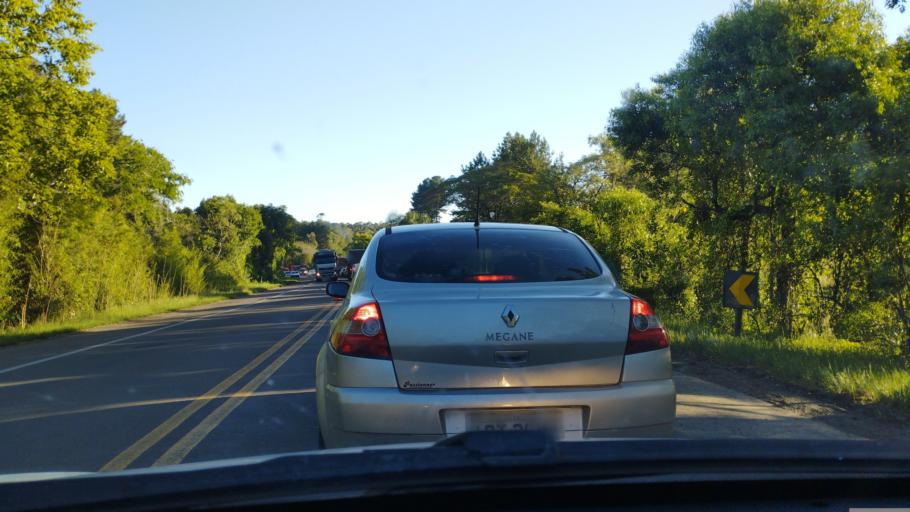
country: BR
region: Rio Grande do Sul
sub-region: Santa Maria
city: Santa Maria
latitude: -29.5986
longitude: -53.7674
